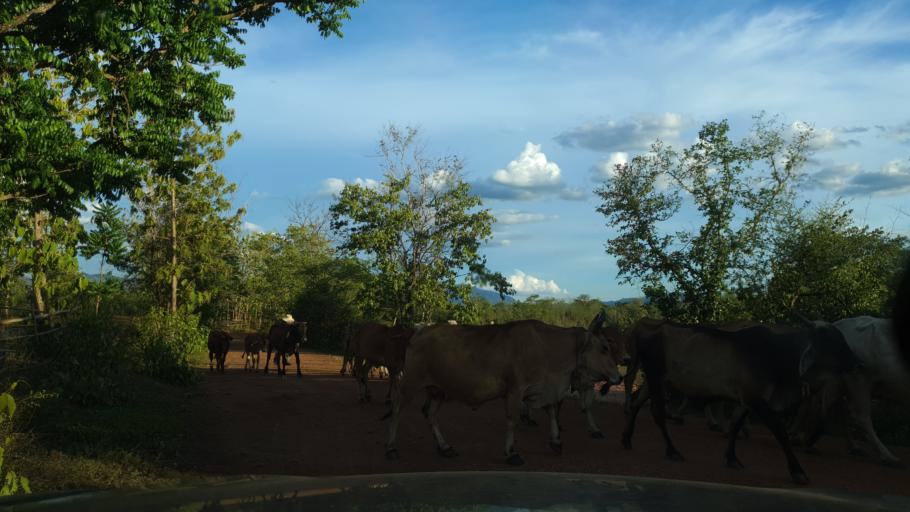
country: TH
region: Lampang
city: Sop Prap
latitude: 17.9589
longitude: 99.3493
